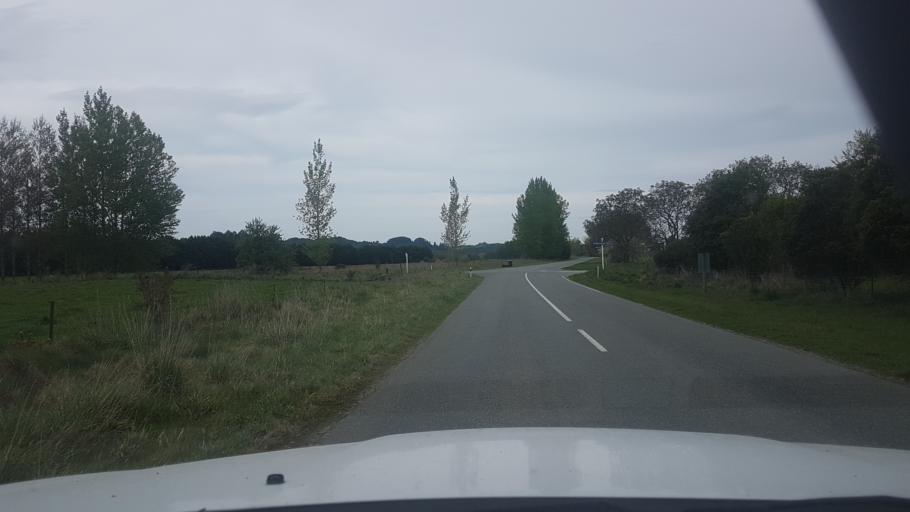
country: NZ
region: Canterbury
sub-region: Timaru District
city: Pleasant Point
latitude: -44.0746
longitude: 171.1698
